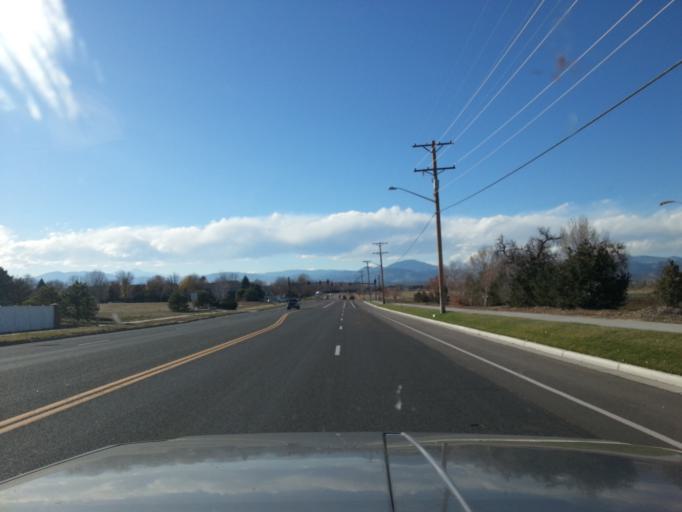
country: US
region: Colorado
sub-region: Larimer County
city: Loveland
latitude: 40.3927
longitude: -105.1135
